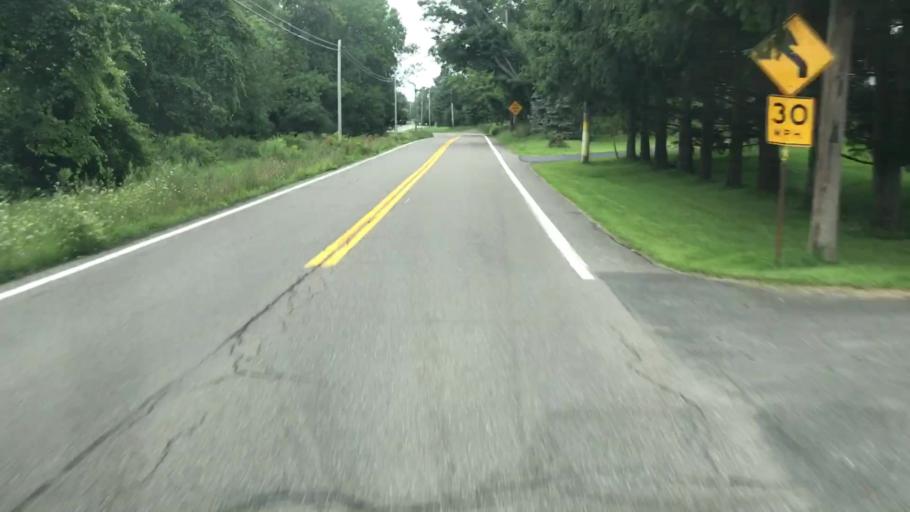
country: US
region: New York
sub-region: Onondaga County
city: Skaneateles
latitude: 42.9839
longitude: -76.4493
